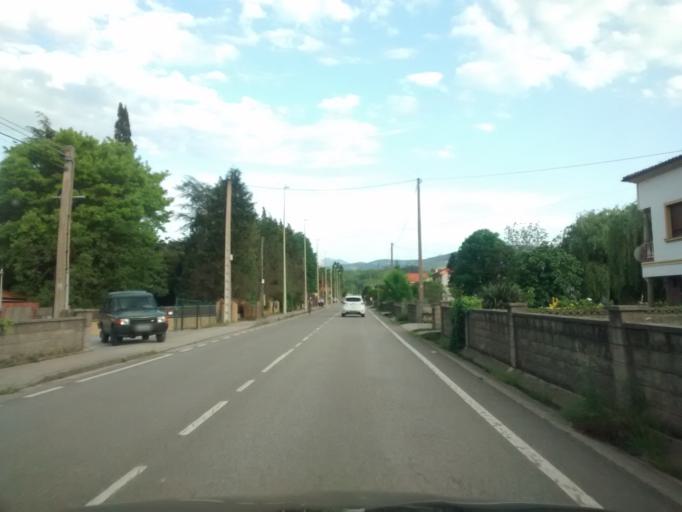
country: ES
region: Cantabria
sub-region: Provincia de Cantabria
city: Entrambasaguas
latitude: 43.3764
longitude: -3.7203
